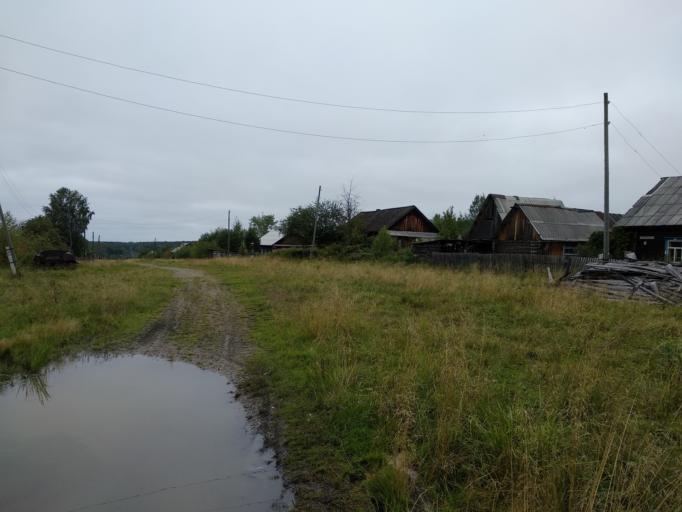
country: RU
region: Sverdlovsk
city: Serov
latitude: 59.8401
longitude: 60.7293
